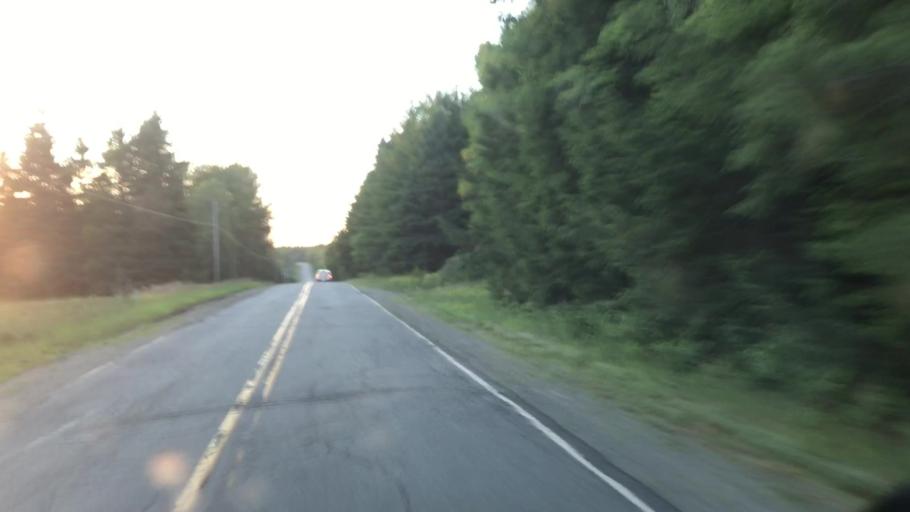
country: US
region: Maine
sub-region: Penobscot County
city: Medway
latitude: 45.5993
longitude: -68.2473
